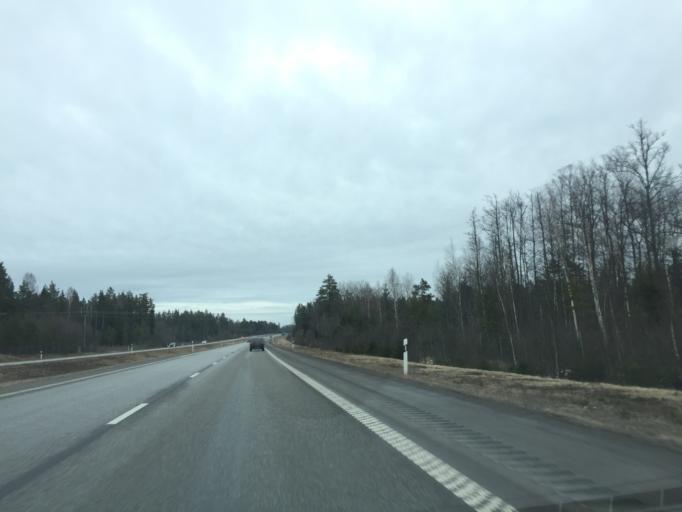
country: SE
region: Vaestmanland
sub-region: Kopings Kommun
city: Koping
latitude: 59.4852
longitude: 15.9132
